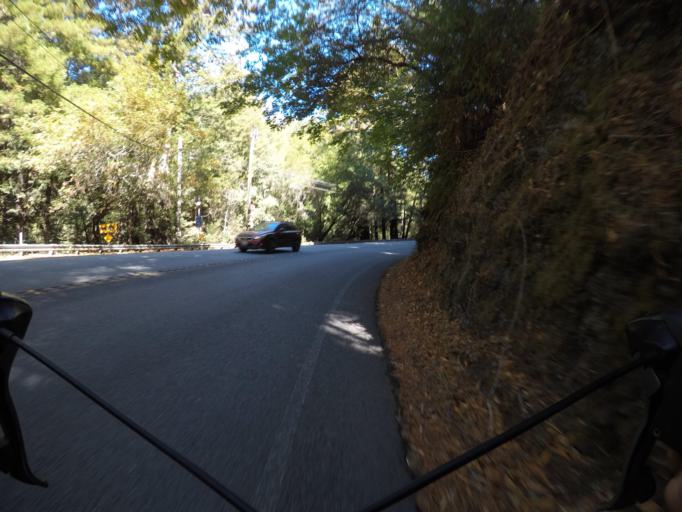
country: US
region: California
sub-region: San Mateo County
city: Portola Valley
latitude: 37.3328
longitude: -122.2712
